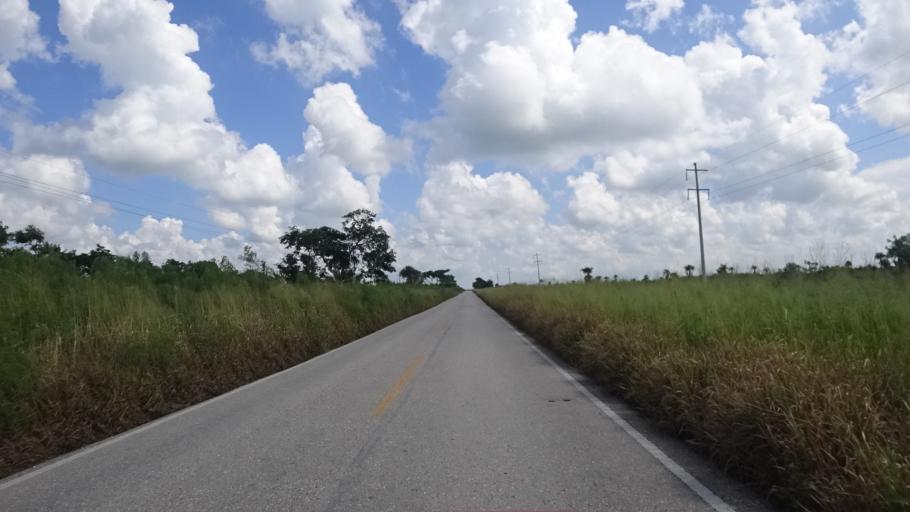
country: MX
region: Yucatan
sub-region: Panaba
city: Loche
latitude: 21.3379
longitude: -88.1587
